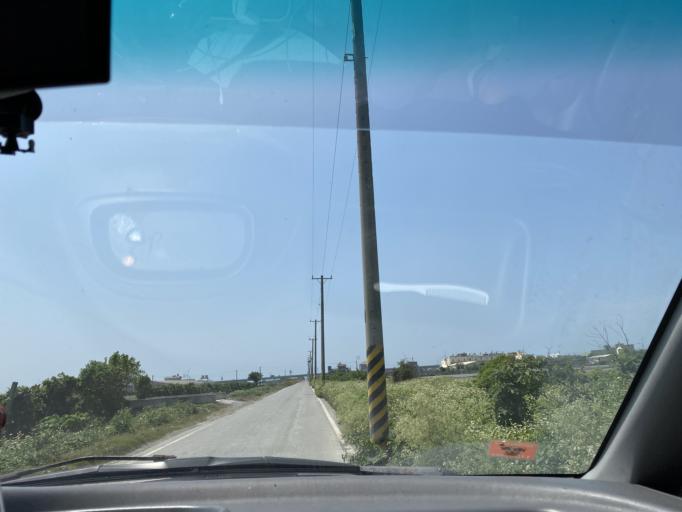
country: TW
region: Taiwan
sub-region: Changhua
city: Chang-hua
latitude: 23.9974
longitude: 120.3887
